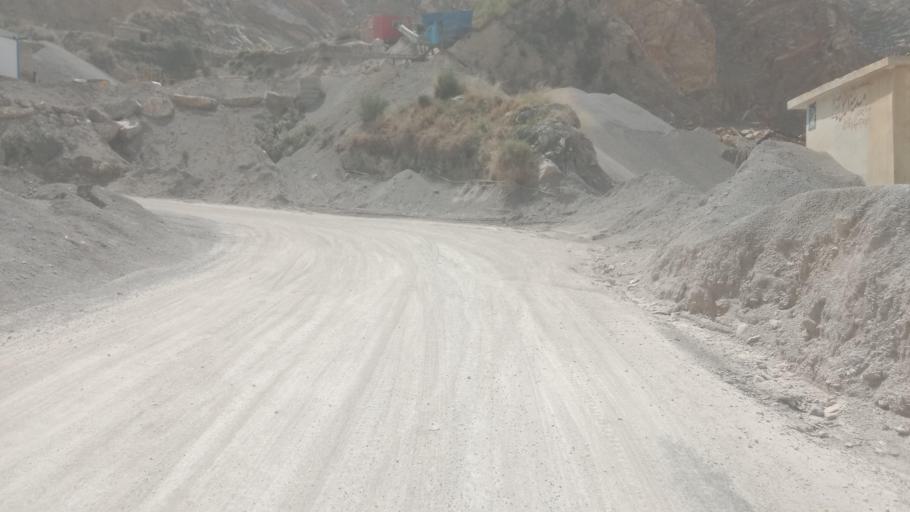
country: PK
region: Khyber Pakhtunkhwa
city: Abbottabad
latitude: 34.1614
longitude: 73.2809
